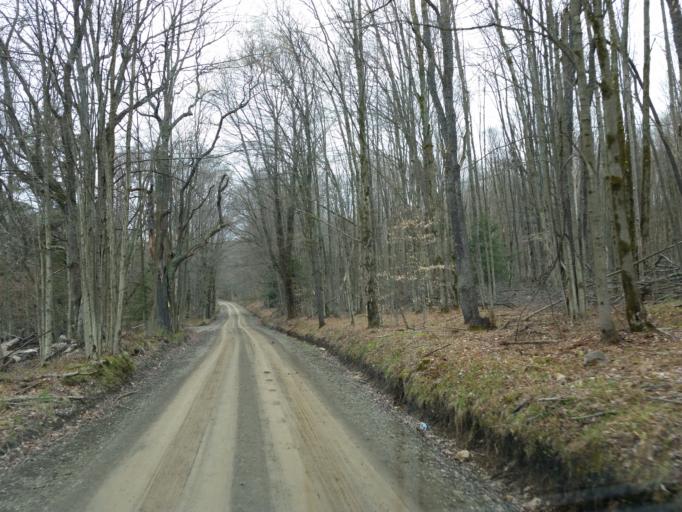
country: US
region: New York
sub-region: Allegany County
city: Andover
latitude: 42.0422
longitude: -77.7452
